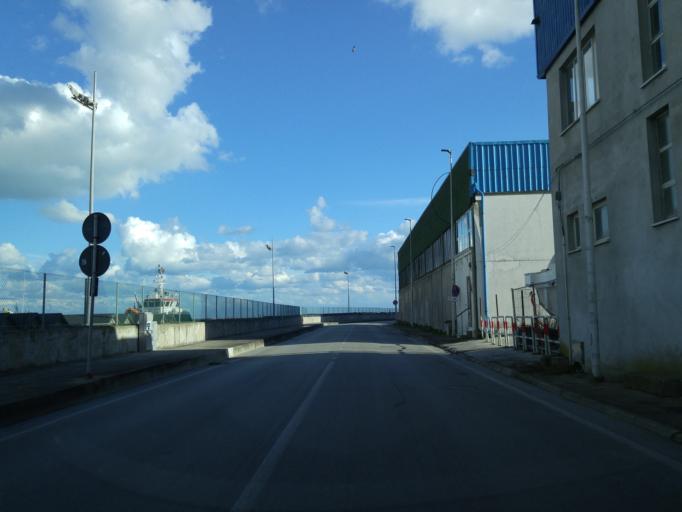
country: IT
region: The Marches
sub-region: Provincia di Pesaro e Urbino
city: Fano
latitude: 43.8518
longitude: 13.0181
